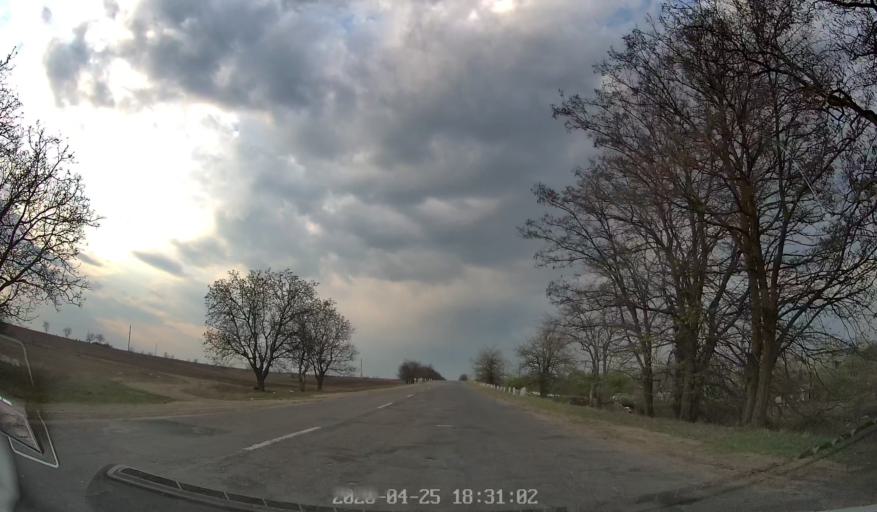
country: MD
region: Criuleni
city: Criuleni
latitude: 47.2128
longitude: 29.1486
